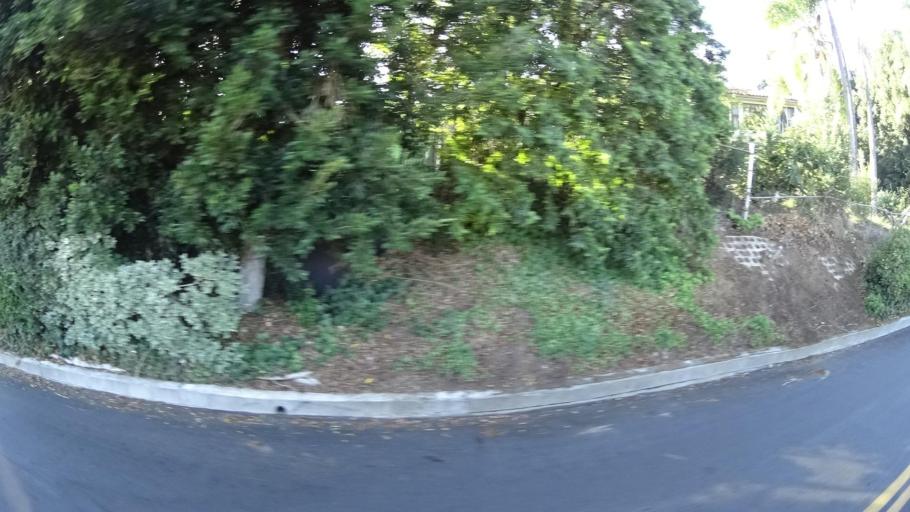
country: US
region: California
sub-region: San Diego County
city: Casa de Oro-Mount Helix
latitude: 32.7712
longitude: -116.9655
